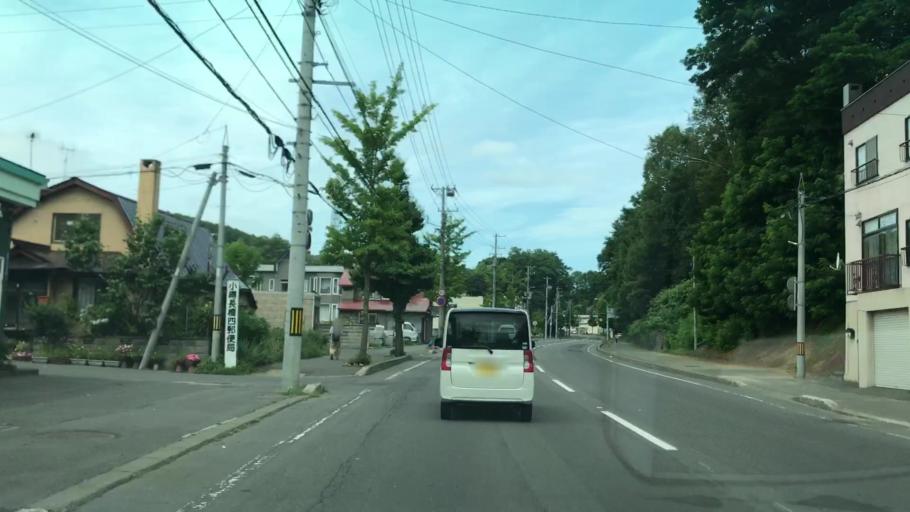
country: JP
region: Hokkaido
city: Otaru
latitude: 43.2101
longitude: 140.9693
